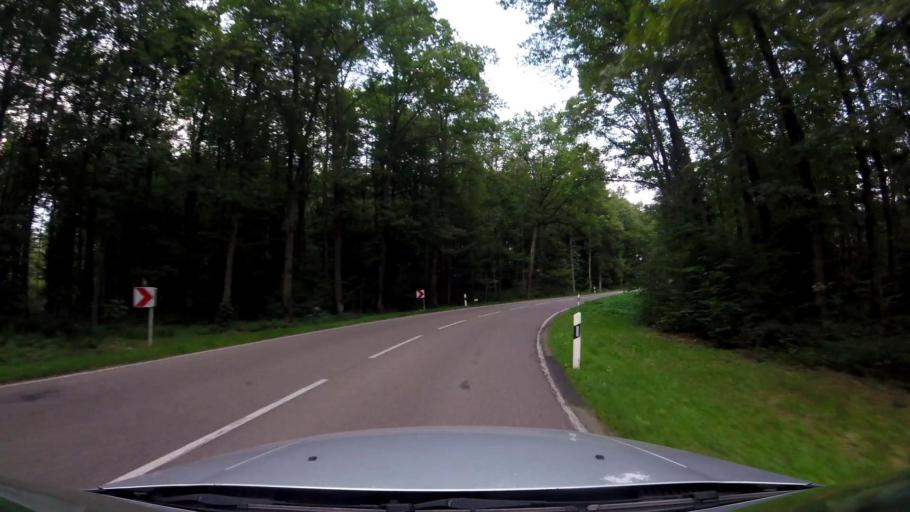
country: DE
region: Baden-Wuerttemberg
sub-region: Regierungsbezirk Stuttgart
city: Rudersberg
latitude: 48.8897
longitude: 9.5017
